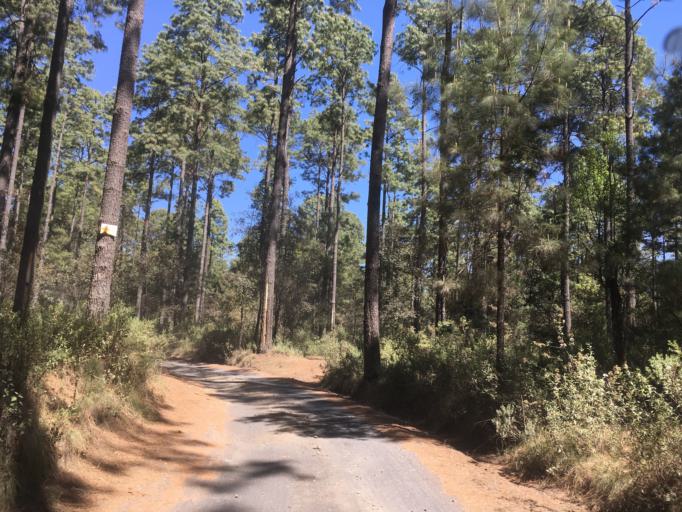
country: MX
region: Michoacan
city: Angahuan
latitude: 19.4627
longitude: -102.2132
